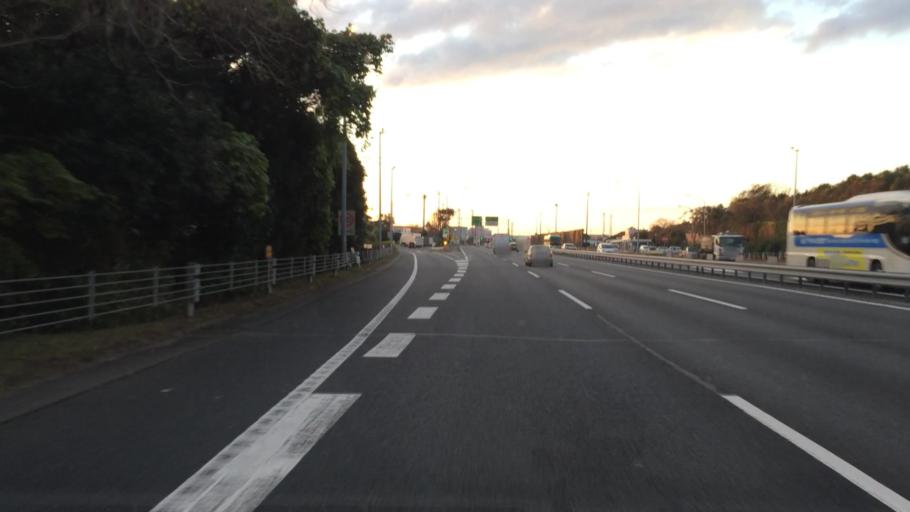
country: JP
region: Chiba
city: Funabashi
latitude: 35.6592
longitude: 140.0323
